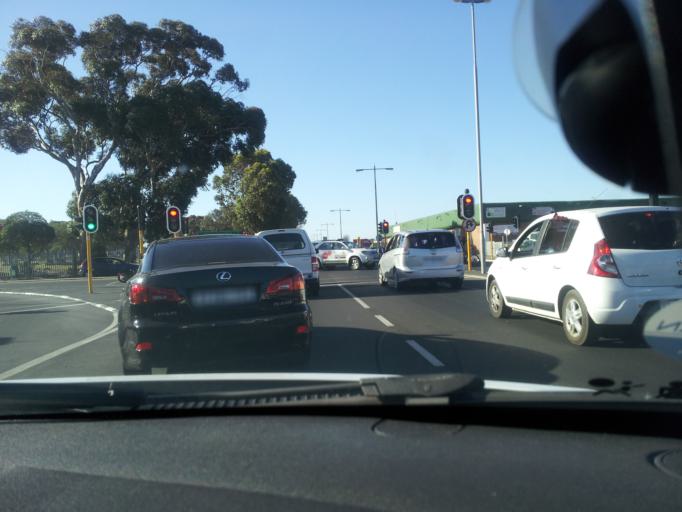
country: ZA
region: Western Cape
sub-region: Overberg District Municipality
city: Grabouw
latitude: -34.1252
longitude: 18.8381
